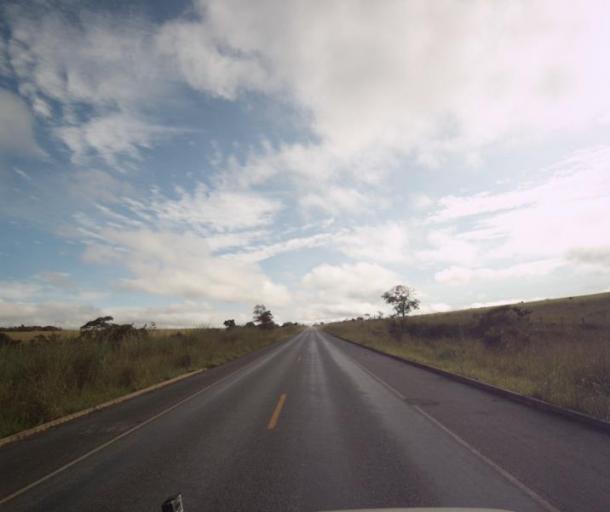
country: BR
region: Goias
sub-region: Padre Bernardo
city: Padre Bernardo
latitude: -15.4752
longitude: -48.6153
